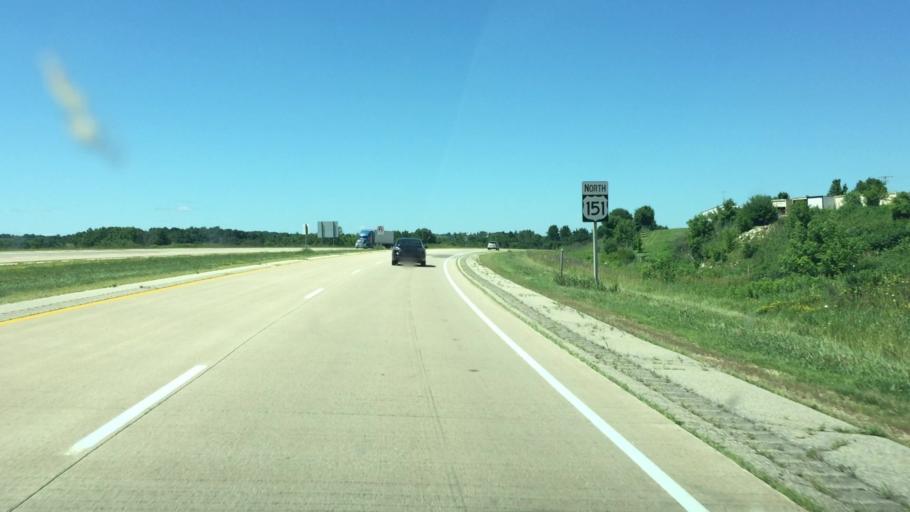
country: US
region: Wisconsin
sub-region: Iowa County
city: Mineral Point
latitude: 42.8572
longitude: -90.2028
